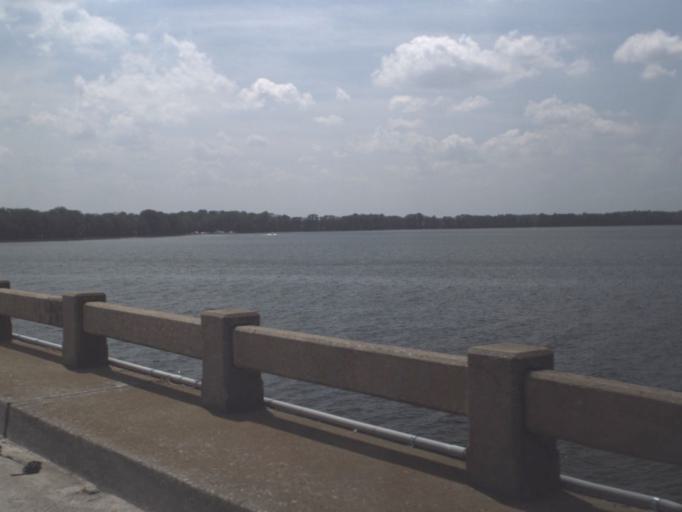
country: US
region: Florida
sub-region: Lake County
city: Howie In The Hills
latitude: 28.7404
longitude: -81.7665
